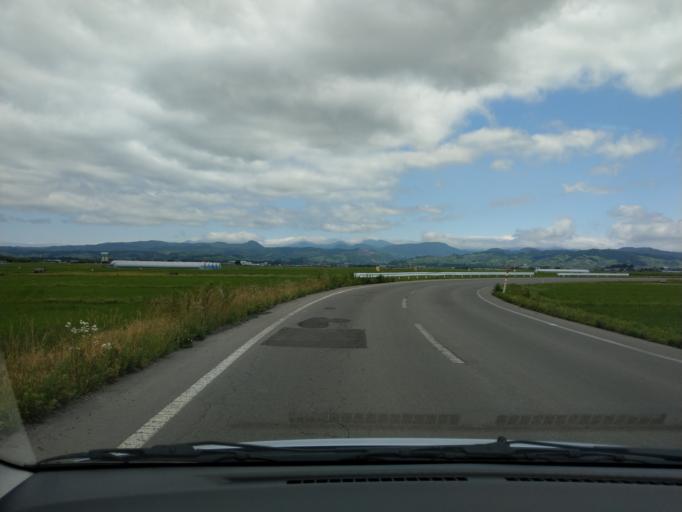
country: JP
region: Aomori
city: Kuroishi
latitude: 40.6302
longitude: 140.5631
